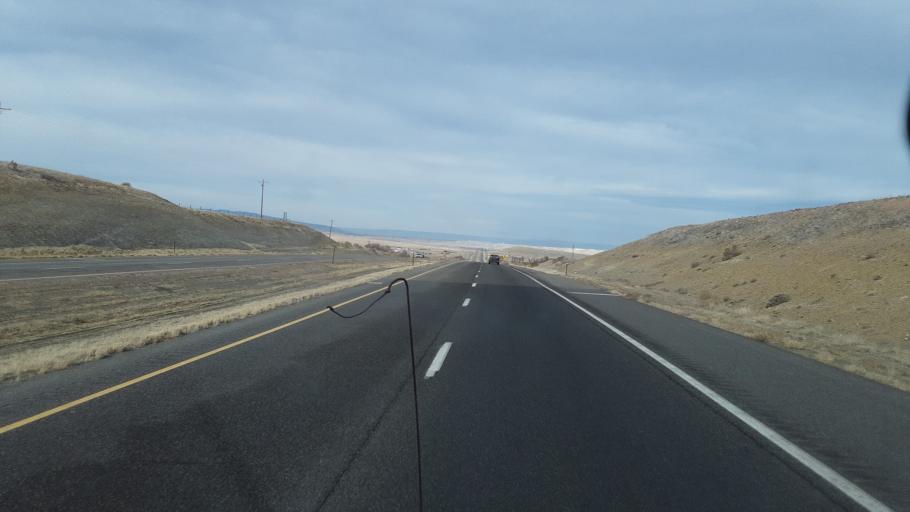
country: US
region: Colorado
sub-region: Mesa County
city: Clifton
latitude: 38.9250
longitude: -108.3832
